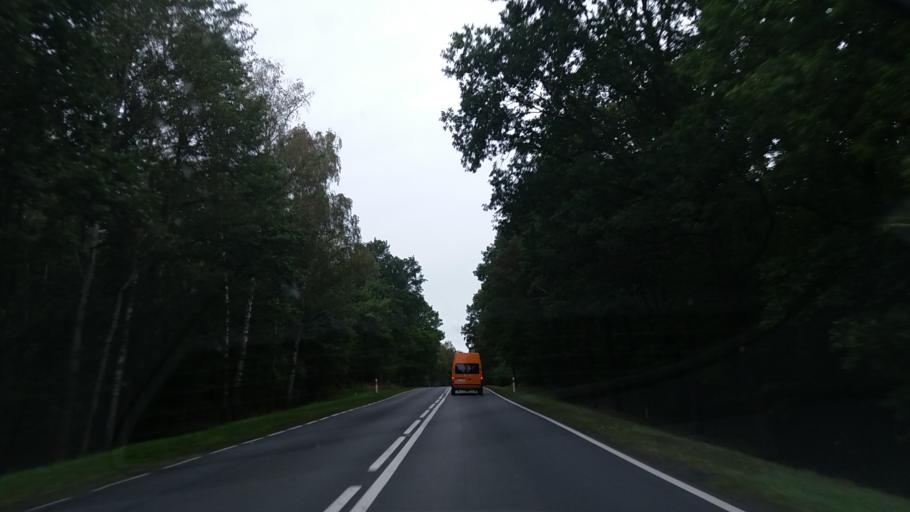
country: PL
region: Lower Silesian Voivodeship
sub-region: Powiat legnicki
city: Prochowice
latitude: 51.2976
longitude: 16.3403
